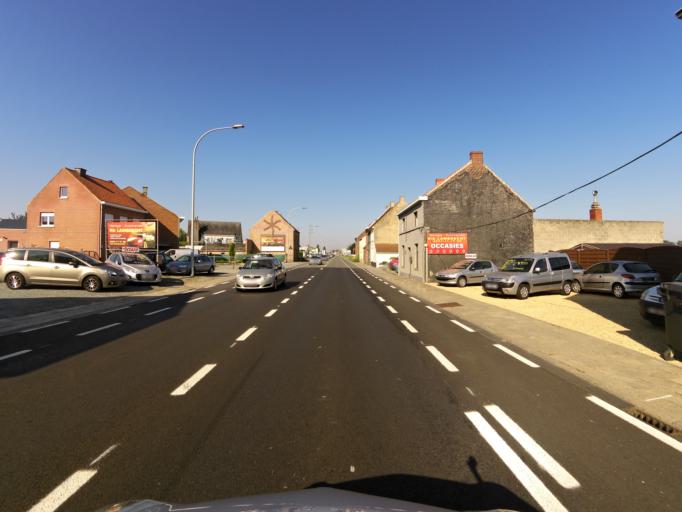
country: BE
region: Flanders
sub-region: Provincie Oost-Vlaanderen
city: Ninove
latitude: 50.8345
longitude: 3.9976
